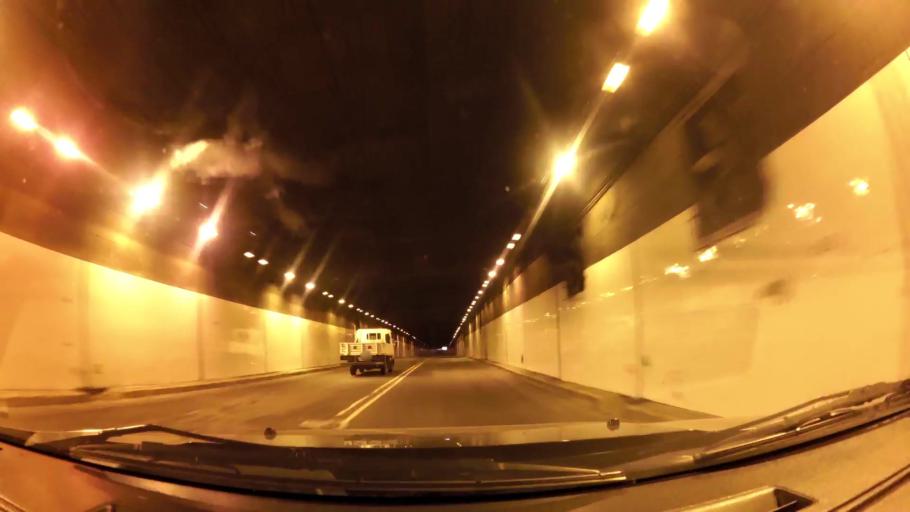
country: EC
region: Pichincha
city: Quito
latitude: -0.2244
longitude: -78.5148
